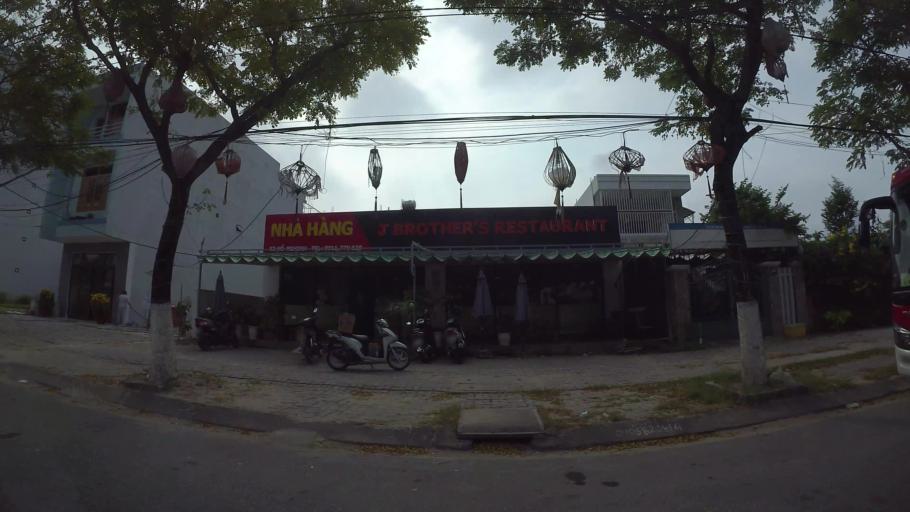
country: VN
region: Da Nang
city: Son Tra
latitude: 16.0777
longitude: 108.2428
